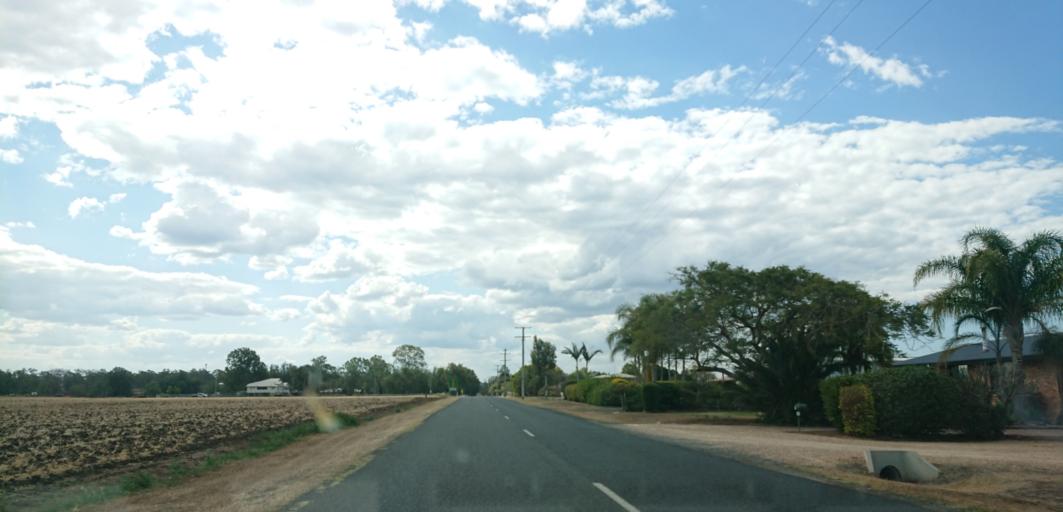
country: AU
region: Queensland
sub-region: Lockyer Valley
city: Gatton
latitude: -27.6118
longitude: 152.2088
